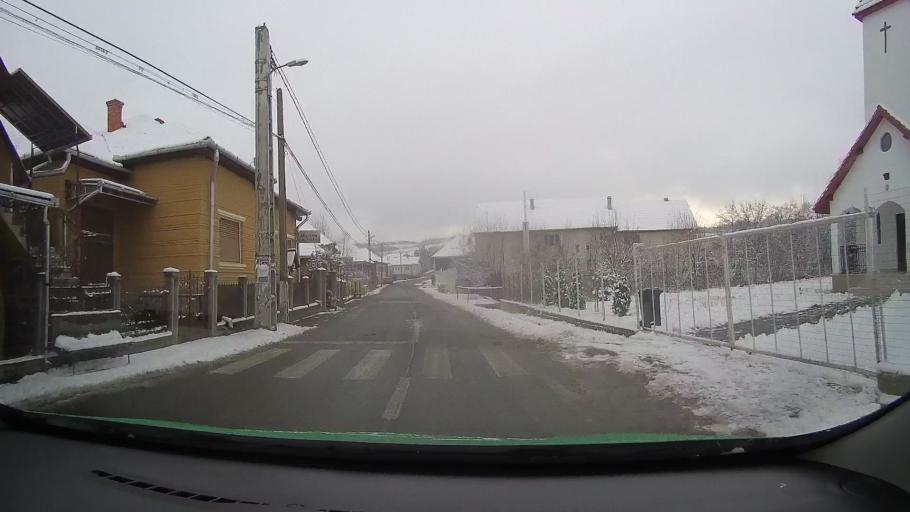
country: RO
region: Hunedoara
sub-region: Oras Hateg
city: Hateg
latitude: 45.6528
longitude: 22.9247
